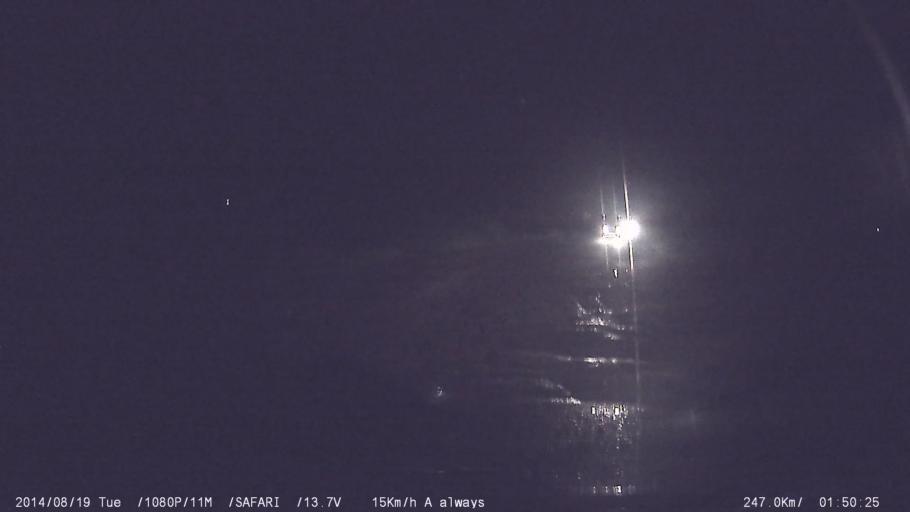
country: IN
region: Tamil Nadu
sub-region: Coimbatore
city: Madukkarai
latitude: 10.8547
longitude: 76.8484
